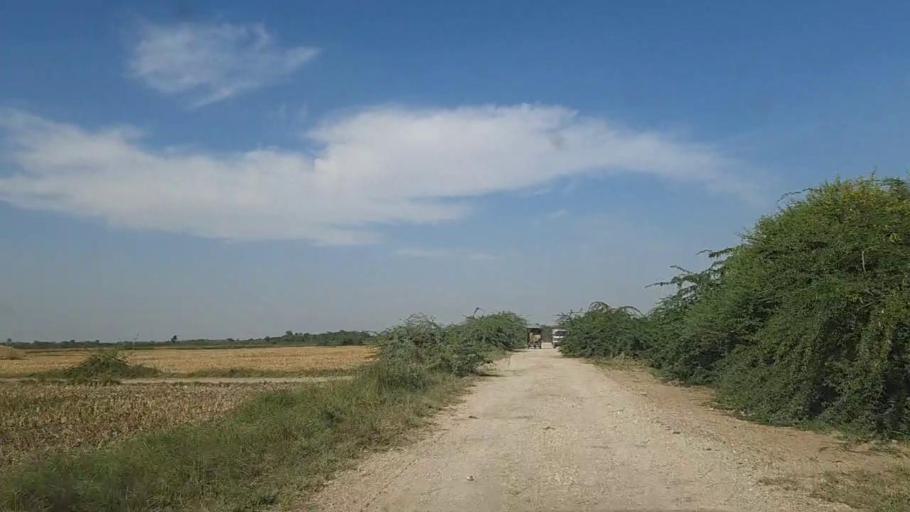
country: PK
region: Sindh
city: Bulri
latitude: 24.8342
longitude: 68.2729
